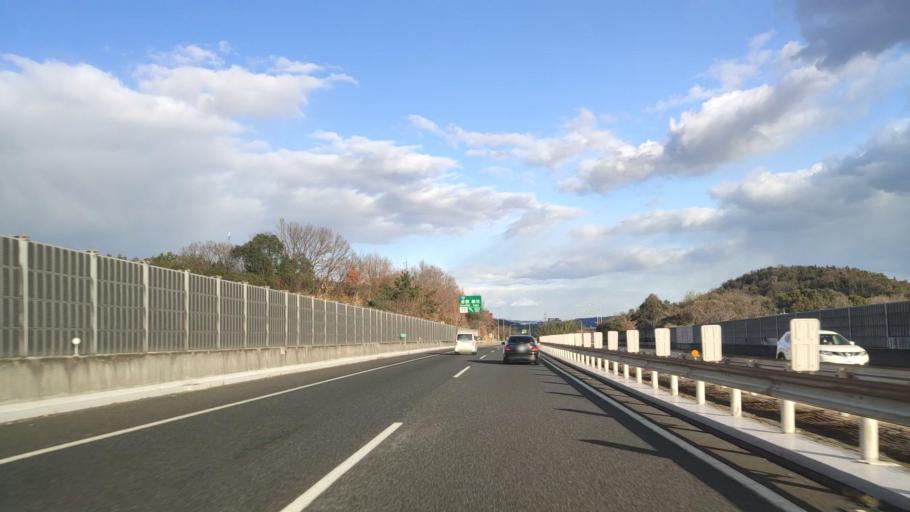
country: JP
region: Okayama
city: Kurashiki
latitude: 34.6257
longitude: 133.7636
